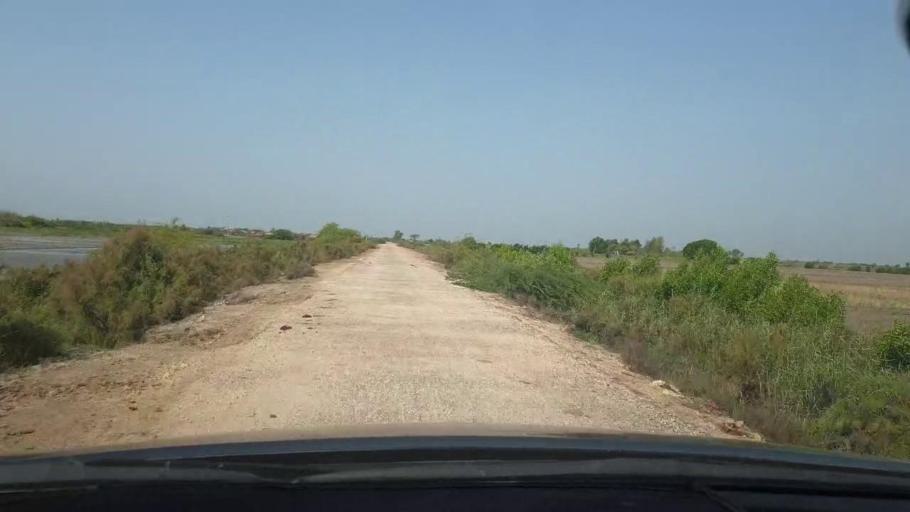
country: PK
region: Sindh
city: Tando Bago
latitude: 24.7092
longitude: 69.1186
